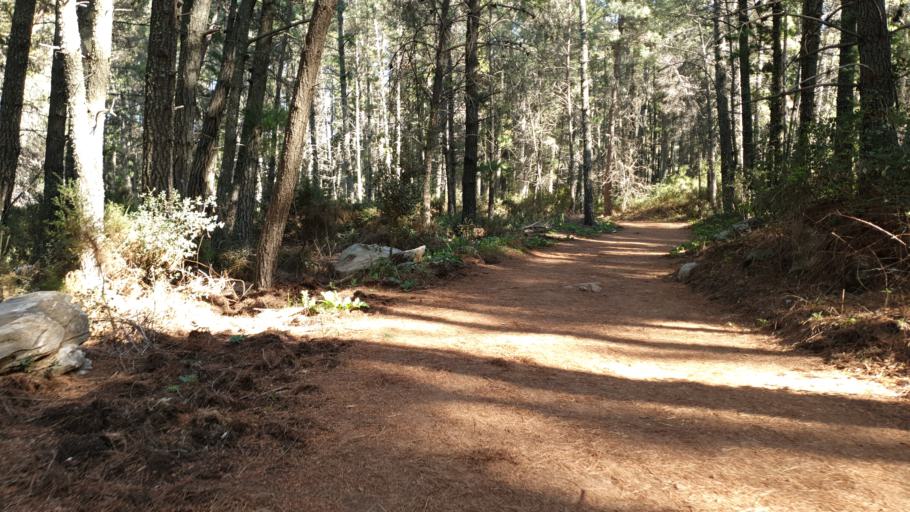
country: ES
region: Andalusia
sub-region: Provincia de Malaga
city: Ojen
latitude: 36.5725
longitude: -4.8933
